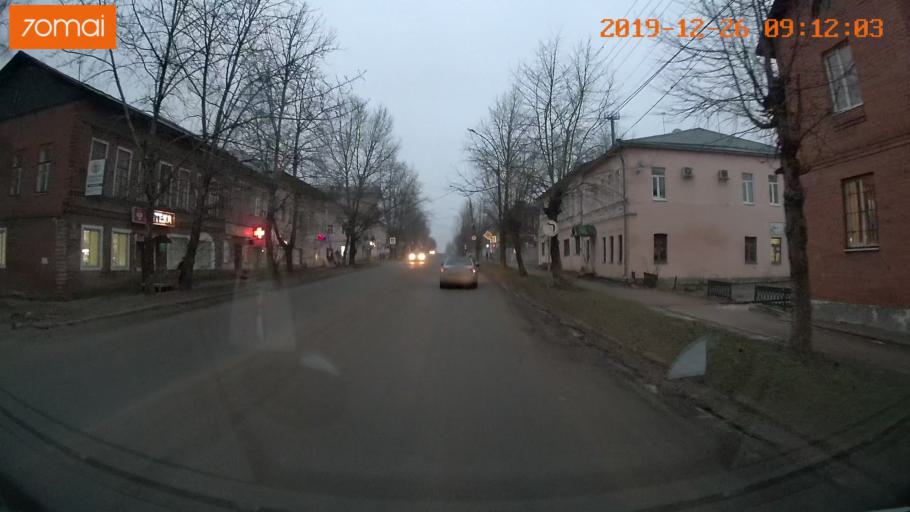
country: RU
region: Vologda
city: Gryazovets
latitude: 58.8790
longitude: 40.2531
